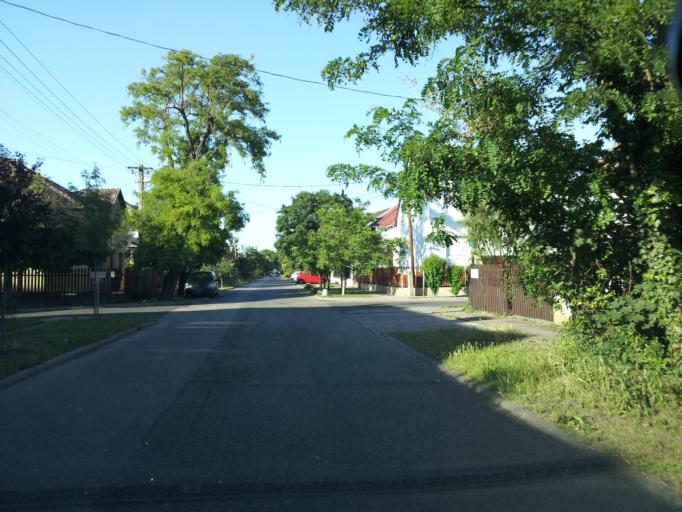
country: HU
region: Budapest
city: Budapest XIV. keruelet
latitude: 47.5328
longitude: 19.1277
